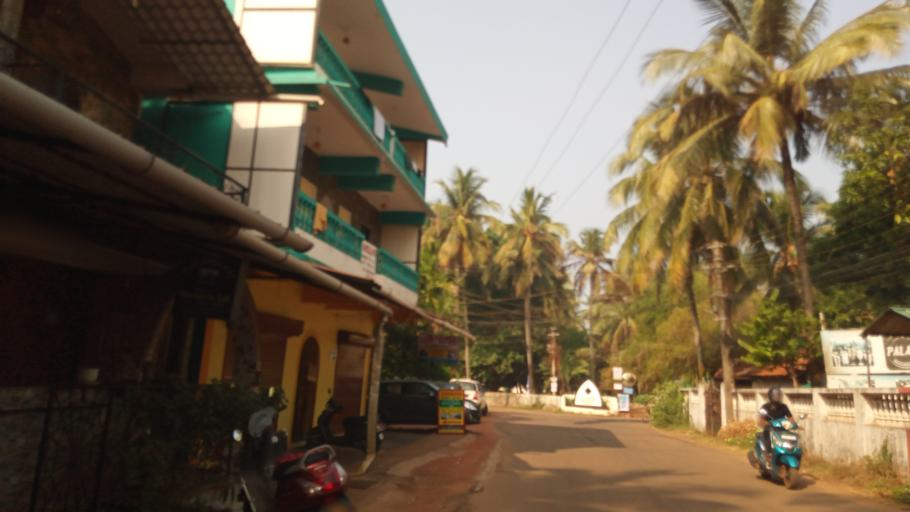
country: IN
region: Goa
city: Calangute
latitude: 15.5389
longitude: 73.7621
